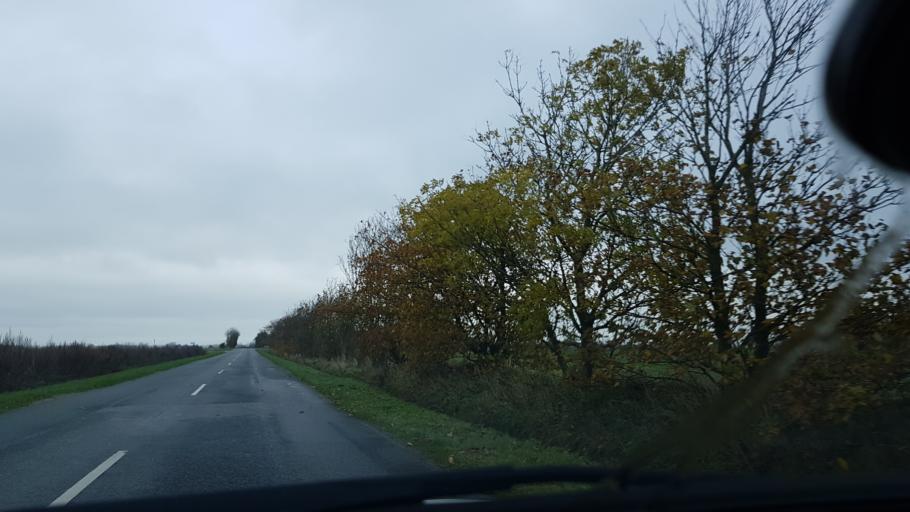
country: DK
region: South Denmark
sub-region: Tonder Kommune
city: Sherrebek
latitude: 55.2199
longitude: 8.8315
